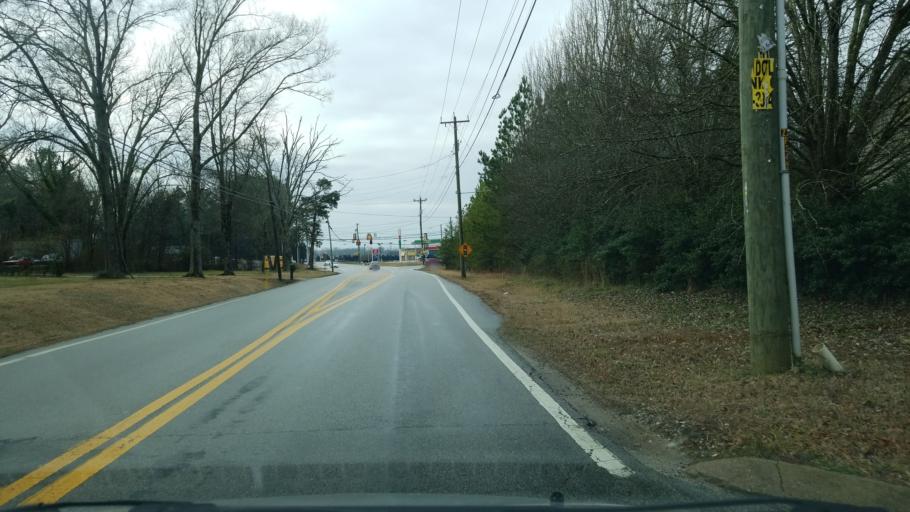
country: US
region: Tennessee
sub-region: Hamilton County
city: East Brainerd
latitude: 35.0011
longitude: -85.0942
